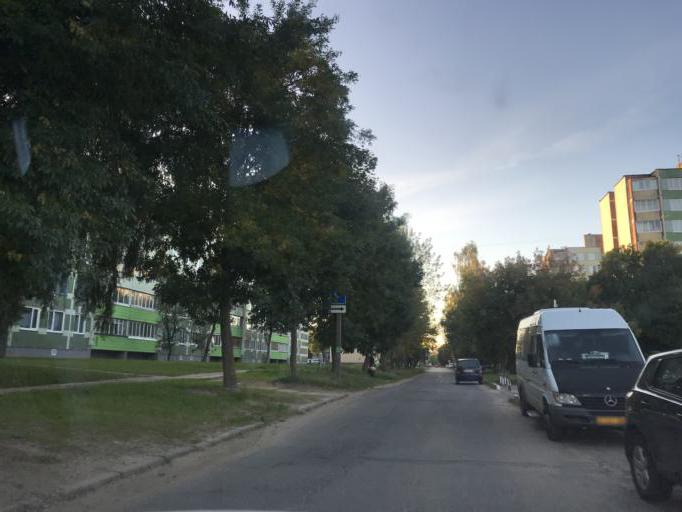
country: BY
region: Mogilev
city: Mahilyow
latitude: 53.9060
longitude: 30.3225
